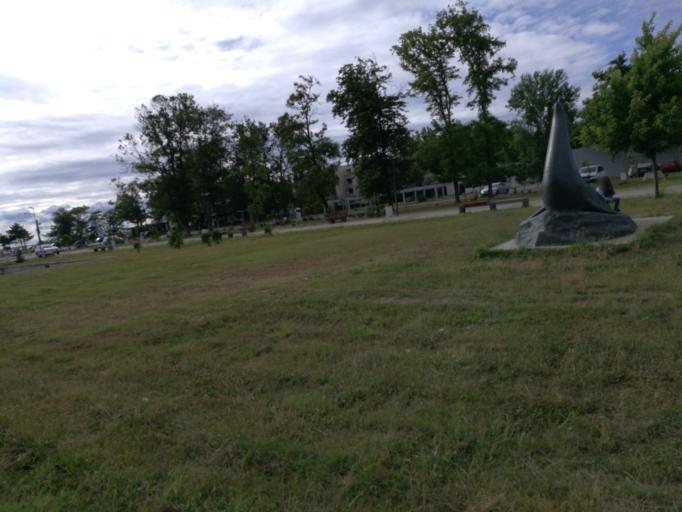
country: RO
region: Constanta
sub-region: Municipiul Constanta
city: Palazu Mare
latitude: 44.2477
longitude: 28.6216
